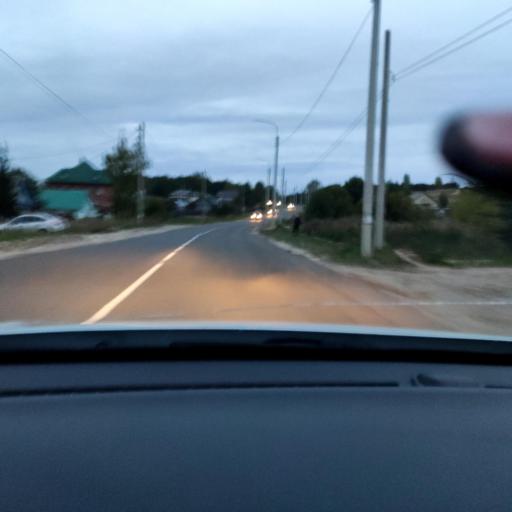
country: RU
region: Mariy-El
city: Volzhsk
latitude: 55.8719
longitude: 48.3726
